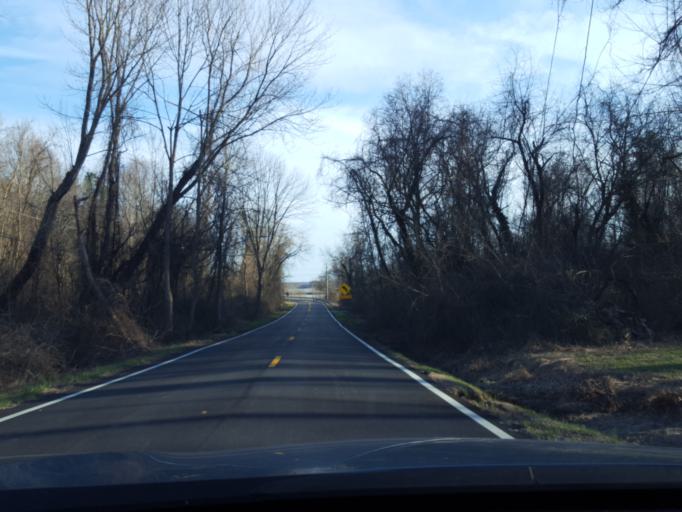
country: US
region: Maryland
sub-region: Anne Arundel County
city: Deale
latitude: 38.7533
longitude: -76.5595
